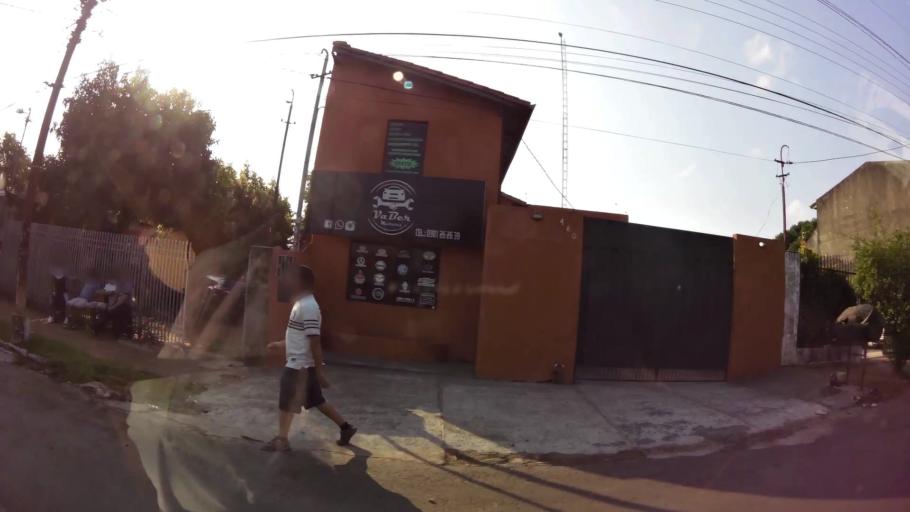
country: PY
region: Central
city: Villa Elisa
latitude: -25.3473
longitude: -57.5844
